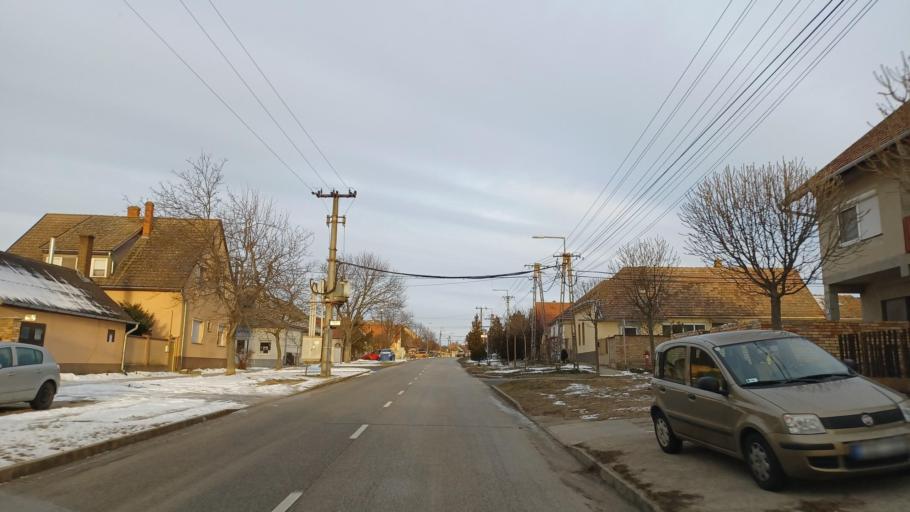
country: HU
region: Tolna
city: Paks
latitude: 46.6304
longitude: 18.8544
